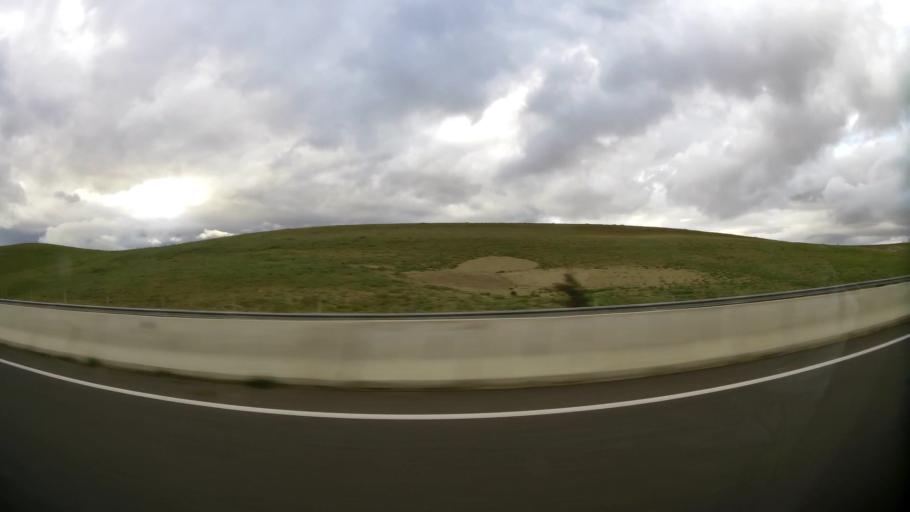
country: MA
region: Taza-Al Hoceima-Taounate
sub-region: Taza
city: Taza
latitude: 34.2575
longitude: -3.8576
